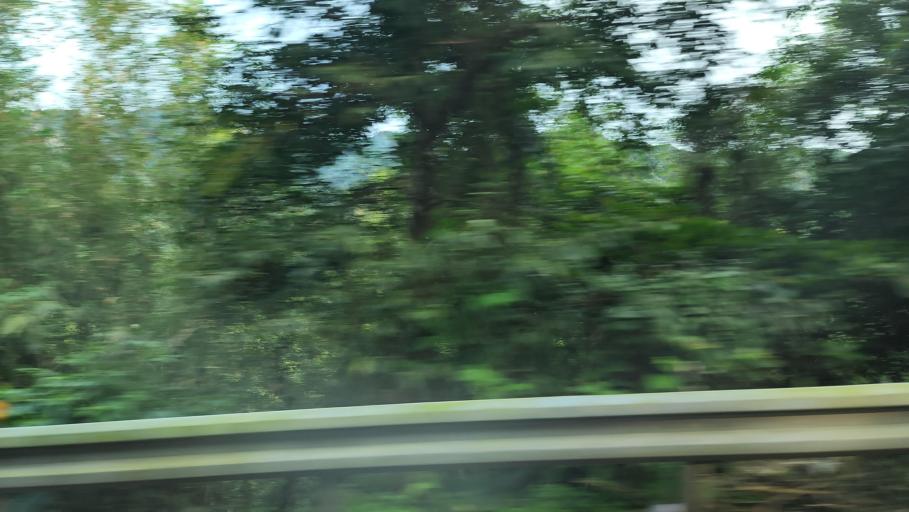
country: TW
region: Taiwan
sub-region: Keelung
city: Keelung
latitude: 25.1604
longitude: 121.6511
